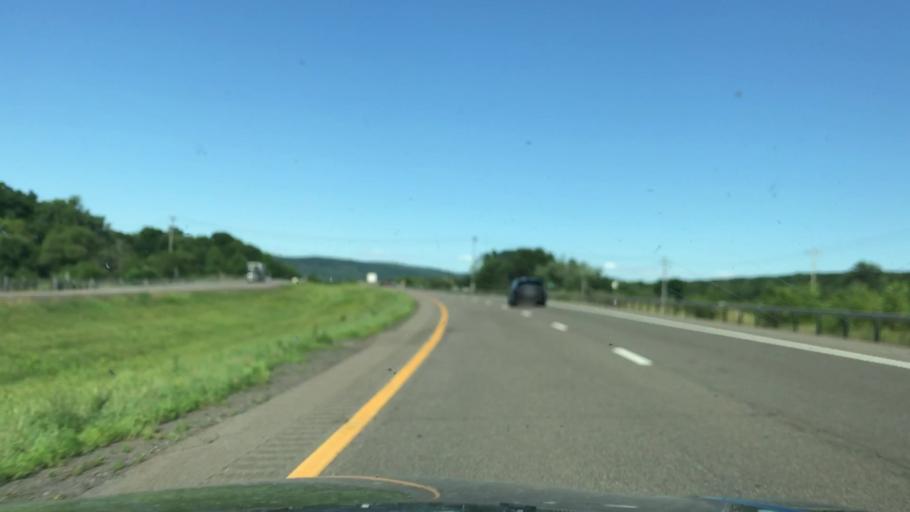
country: US
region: New York
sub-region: Tioga County
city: Apalachin
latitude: 42.0802
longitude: -76.2062
